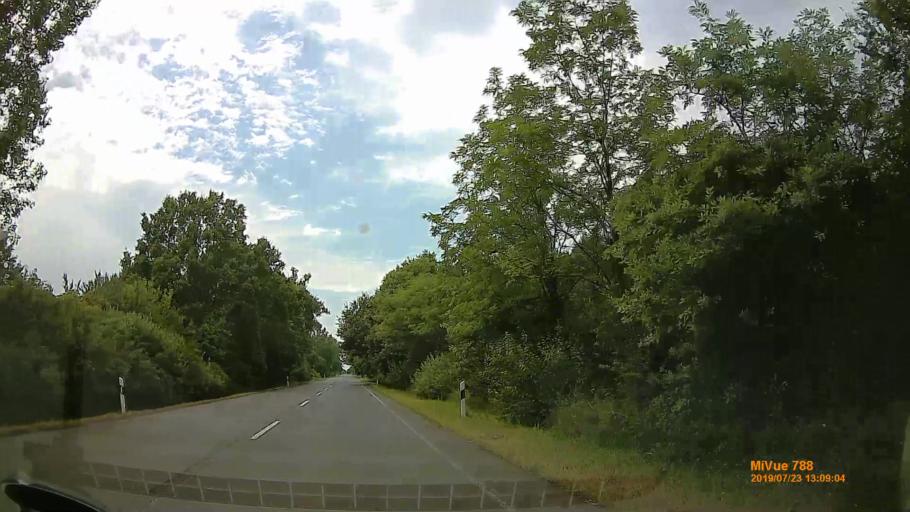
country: HU
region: Szabolcs-Szatmar-Bereg
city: Tiszavasvari
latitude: 47.9403
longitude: 21.3128
